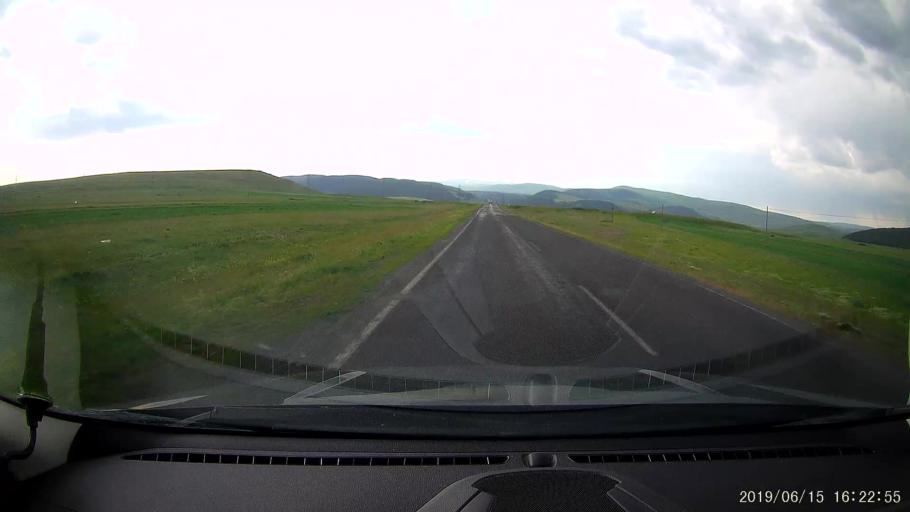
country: TR
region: Ardahan
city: Hanak
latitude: 41.1834
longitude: 42.8560
